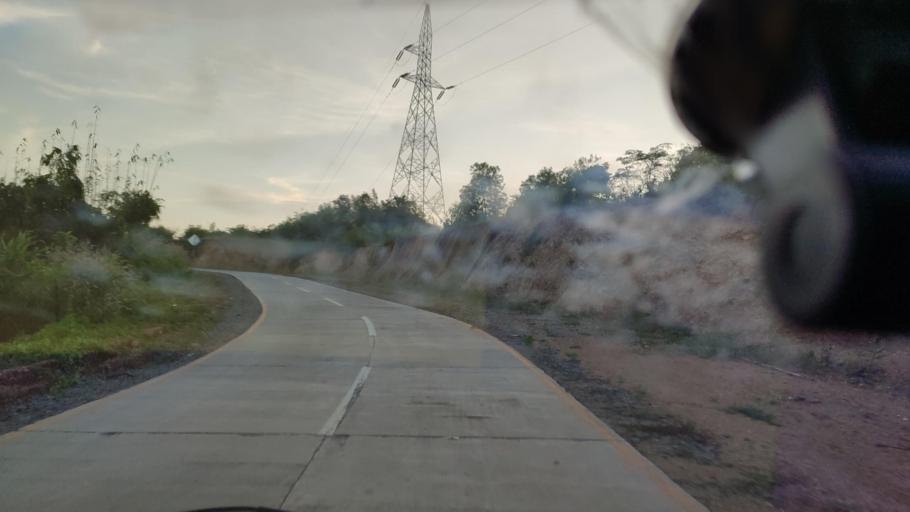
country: MM
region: Magway
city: Minbu
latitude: 19.8235
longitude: 94.0731
